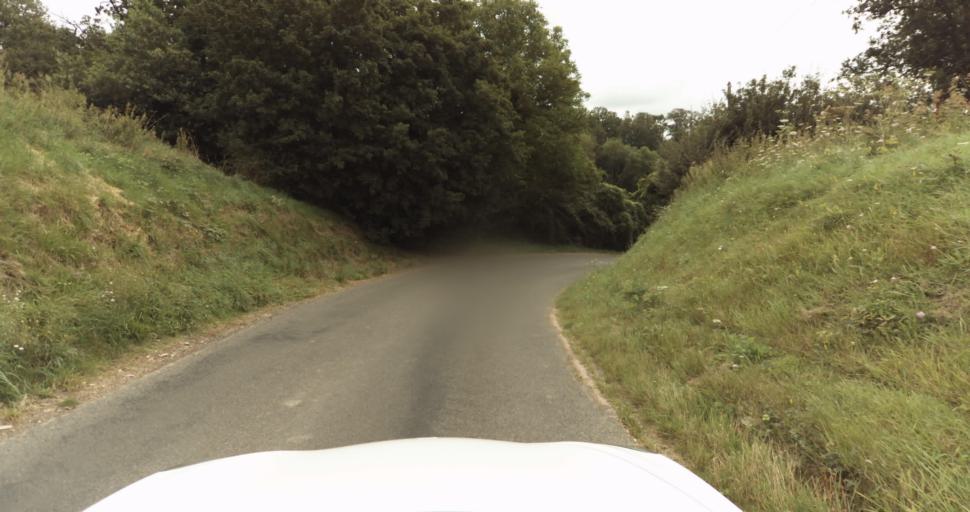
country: FR
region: Haute-Normandie
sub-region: Departement de l'Eure
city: Saint-Sebastien-de-Morsent
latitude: 49.0161
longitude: 1.0622
